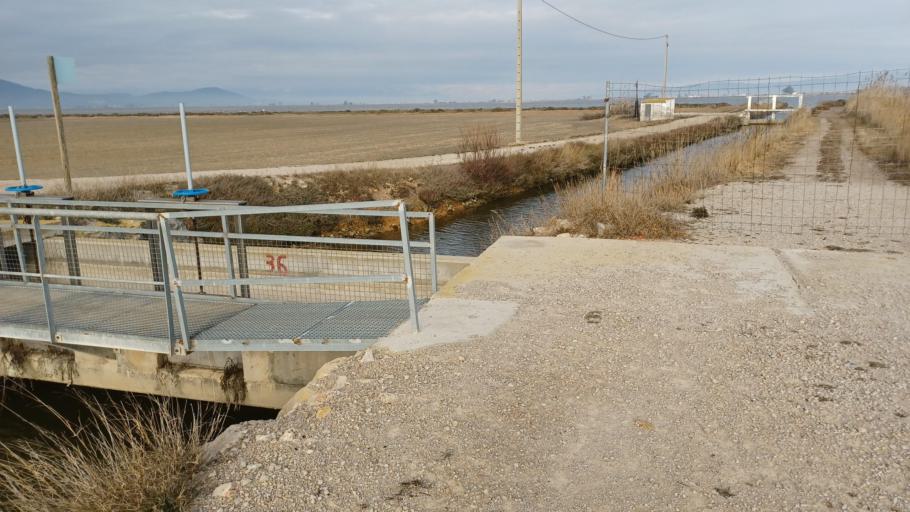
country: ES
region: Catalonia
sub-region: Provincia de Tarragona
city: Deltebre
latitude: 40.6455
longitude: 0.6801
